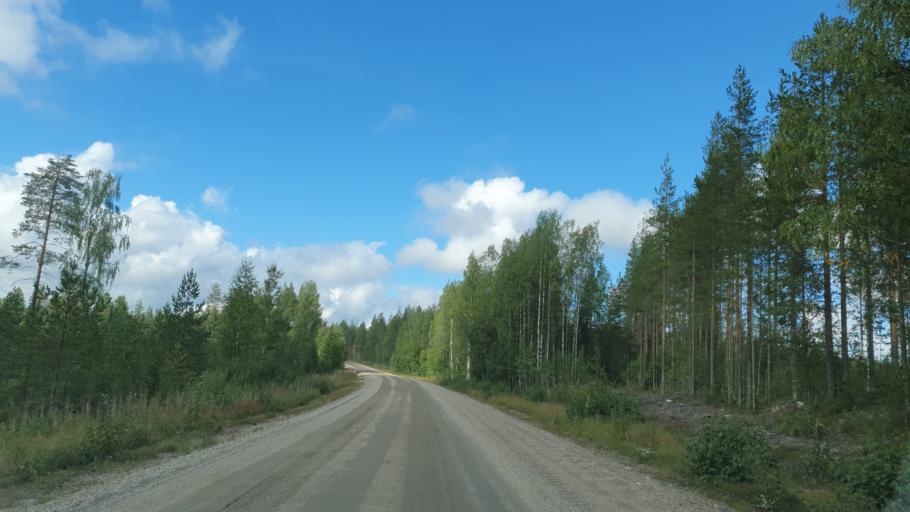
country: FI
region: Kainuu
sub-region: Kehys-Kainuu
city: Kuhmo
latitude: 63.9833
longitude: 29.2453
